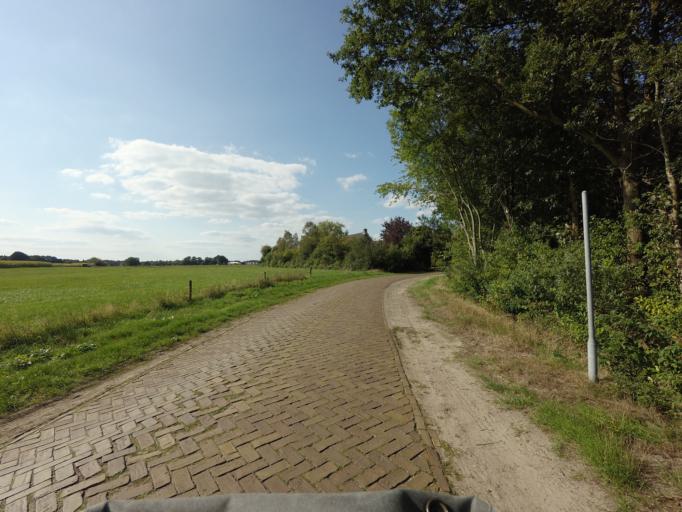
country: NL
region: Drenthe
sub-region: Gemeente Westerveld
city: Dwingeloo
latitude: 52.8344
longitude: 6.3921
